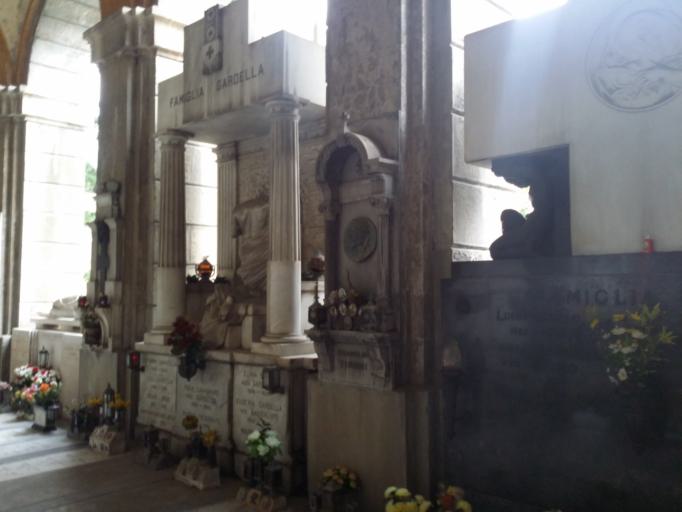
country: IT
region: Liguria
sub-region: Provincia di Genova
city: Genoa
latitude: 44.4291
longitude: 8.9483
